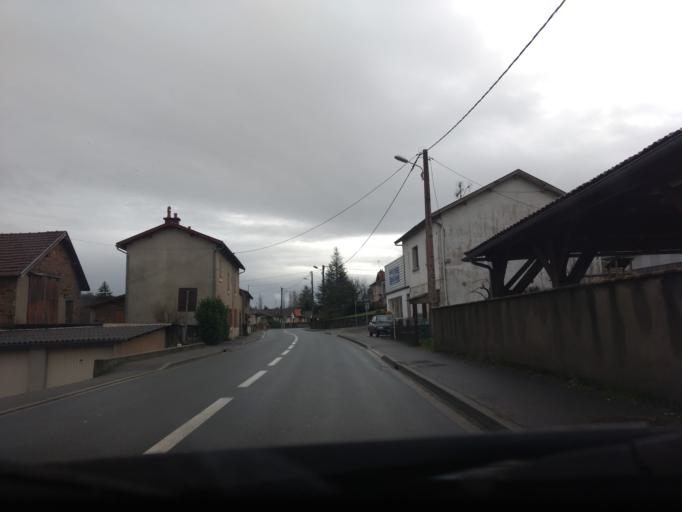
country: FR
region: Midi-Pyrenees
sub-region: Departement de l'Aveyron
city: Firmi
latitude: 44.5341
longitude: 2.3199
